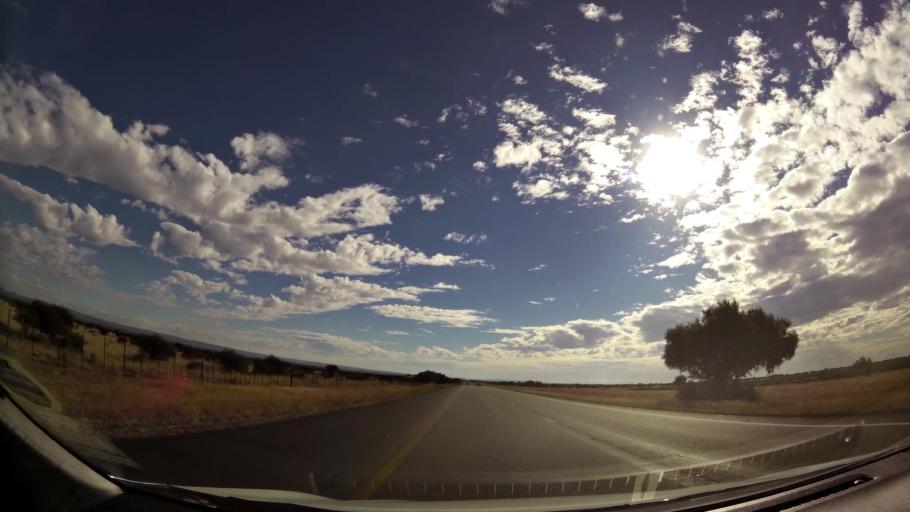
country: ZA
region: Limpopo
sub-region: Waterberg District Municipality
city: Bela-Bela
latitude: -25.0101
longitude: 28.3406
